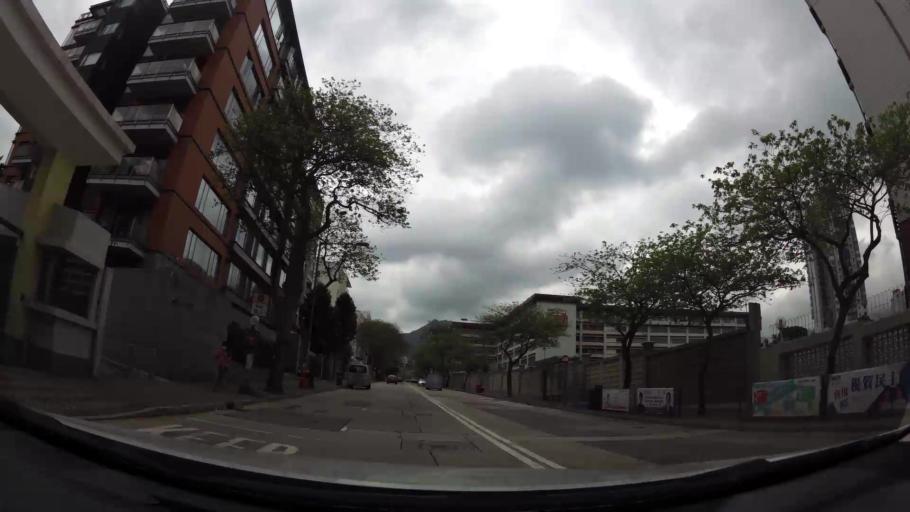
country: HK
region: Kowloon City
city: Kowloon
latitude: 22.3279
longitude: 114.1819
